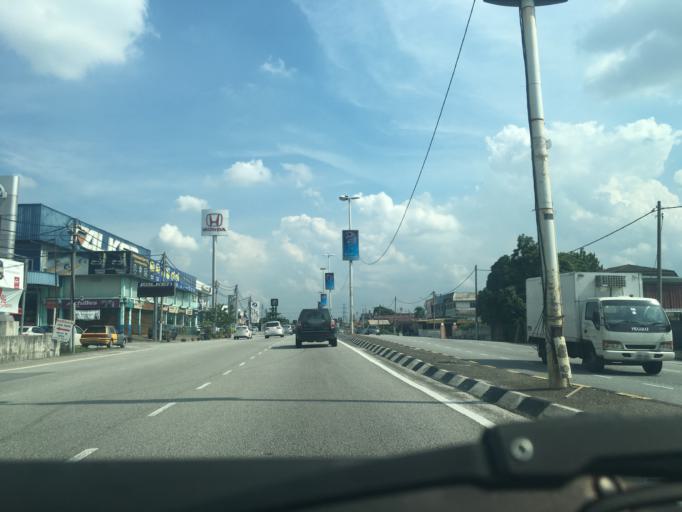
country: MY
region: Perak
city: Ipoh
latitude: 4.6258
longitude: 101.0819
